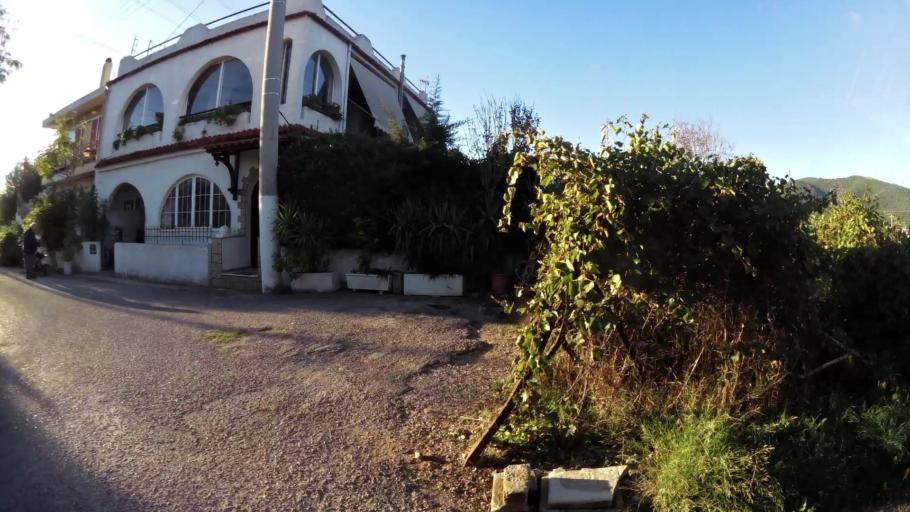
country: GR
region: Attica
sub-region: Nomarchia Anatolikis Attikis
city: Pallini
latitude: 38.0040
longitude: 23.8630
